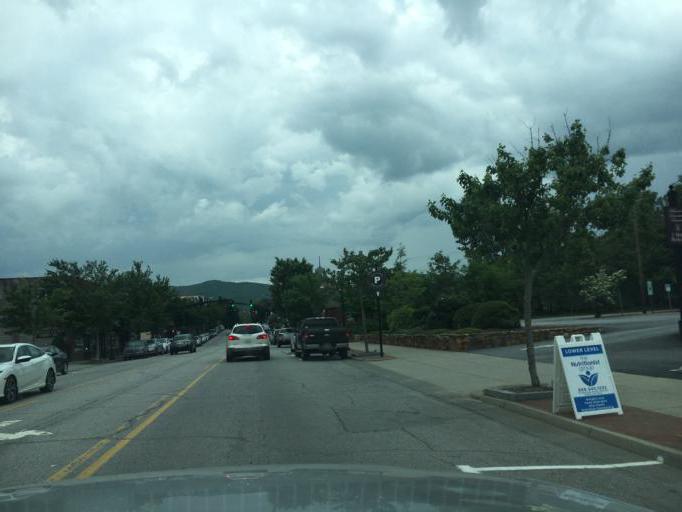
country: US
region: North Carolina
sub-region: Transylvania County
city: Brevard
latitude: 35.2328
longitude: -82.7322
